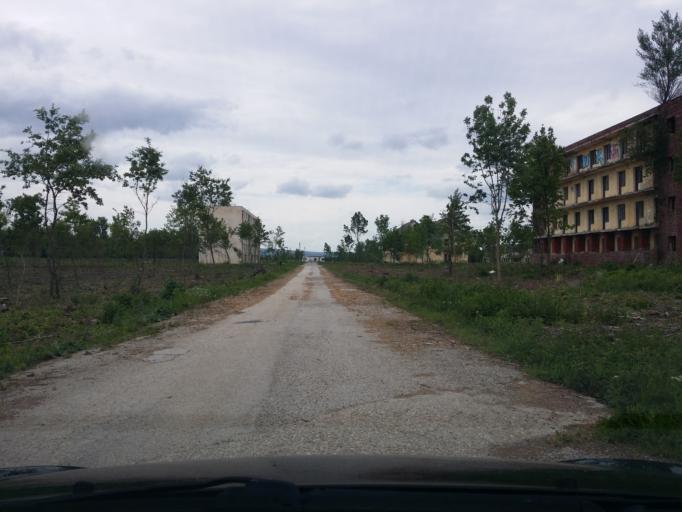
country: HU
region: Veszprem
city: Szentkiralyszabadja
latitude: 47.0828
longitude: 17.9789
